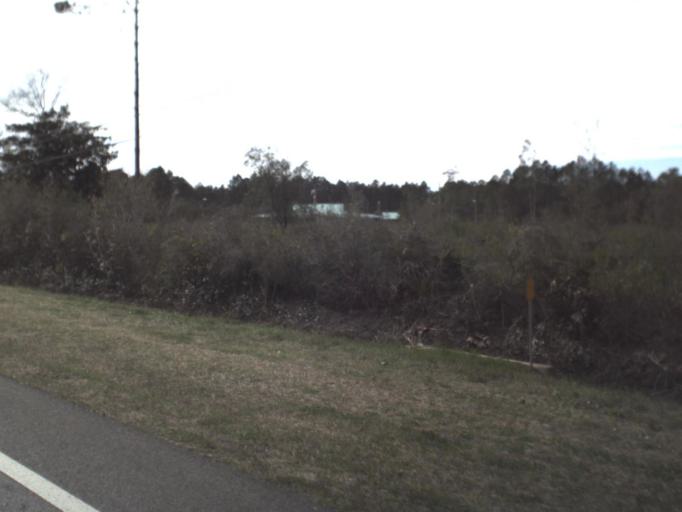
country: US
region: Florida
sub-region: Bay County
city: Hiland Park
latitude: 30.2362
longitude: -85.5751
